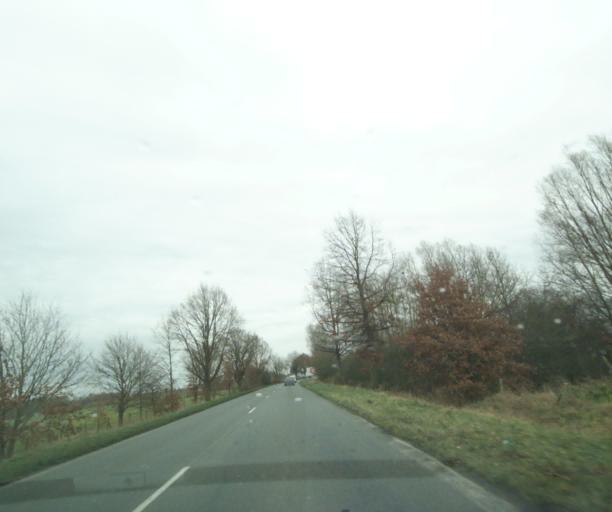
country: FR
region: Nord-Pas-de-Calais
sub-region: Departement du Nord
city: Quarouble
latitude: 50.4019
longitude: 3.6345
